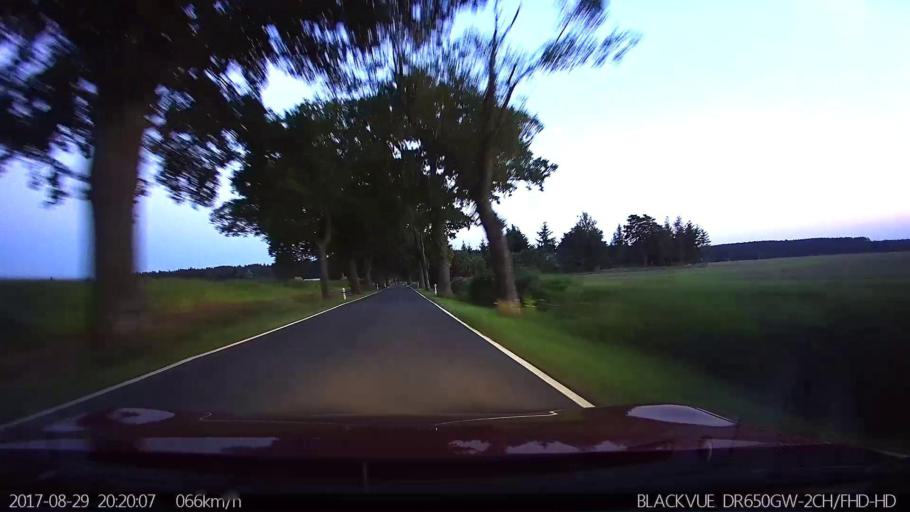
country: DE
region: Mecklenburg-Vorpommern
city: Velgast
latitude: 54.2624
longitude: 12.8204
